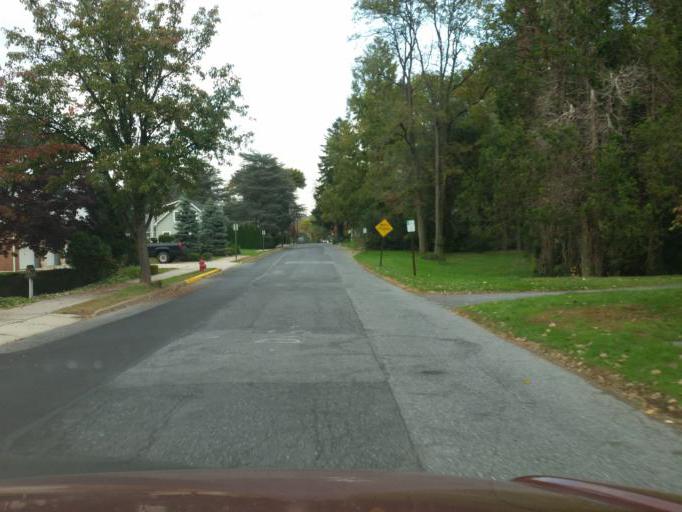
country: US
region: Pennsylvania
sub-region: Dauphin County
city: Hummelstown
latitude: 40.2612
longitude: -76.7052
